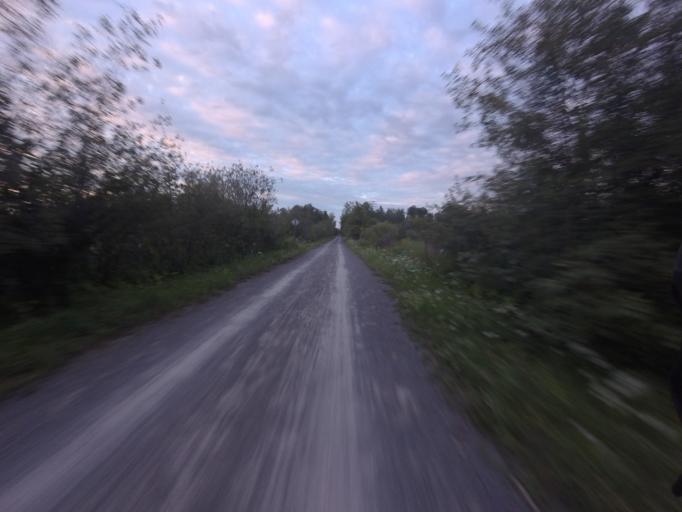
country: CA
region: Ontario
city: Bells Corners
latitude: 45.2317
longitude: -75.9629
